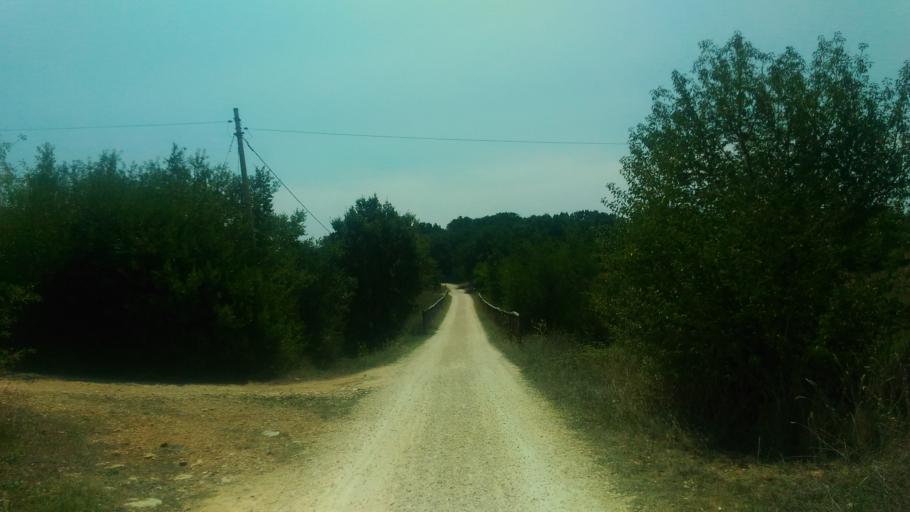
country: IT
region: Apulia
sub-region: Provincia di Brindisi
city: Cisternino
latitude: 40.7339
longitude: 17.3890
